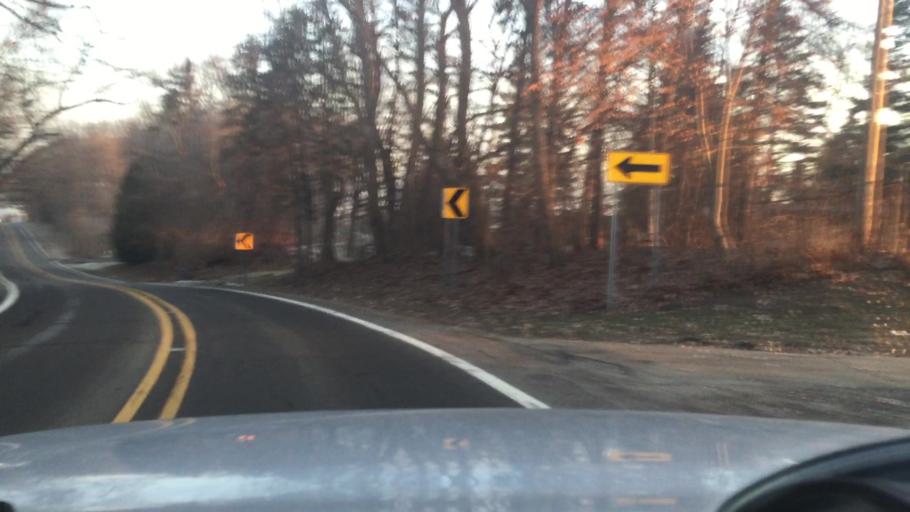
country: US
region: Michigan
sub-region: Oakland County
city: Waterford
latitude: 42.6702
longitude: -83.3571
